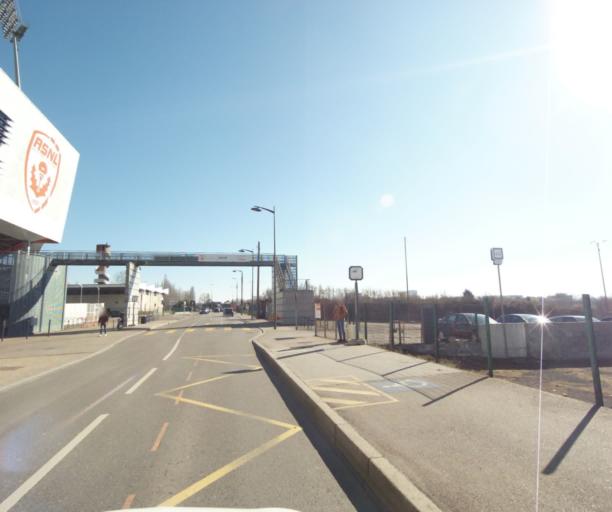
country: FR
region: Lorraine
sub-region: Departement de Meurthe-et-Moselle
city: Saint-Max
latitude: 48.6949
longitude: 6.2099
